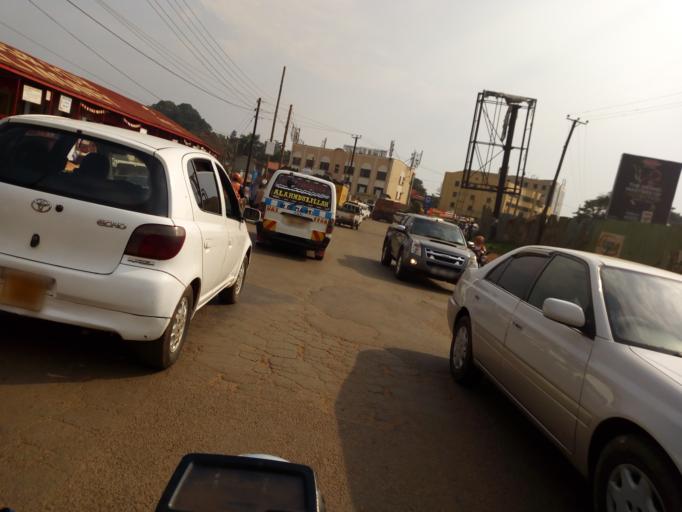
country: UG
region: Central Region
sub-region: Wakiso District
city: Kireka
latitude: 0.3193
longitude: 32.6238
